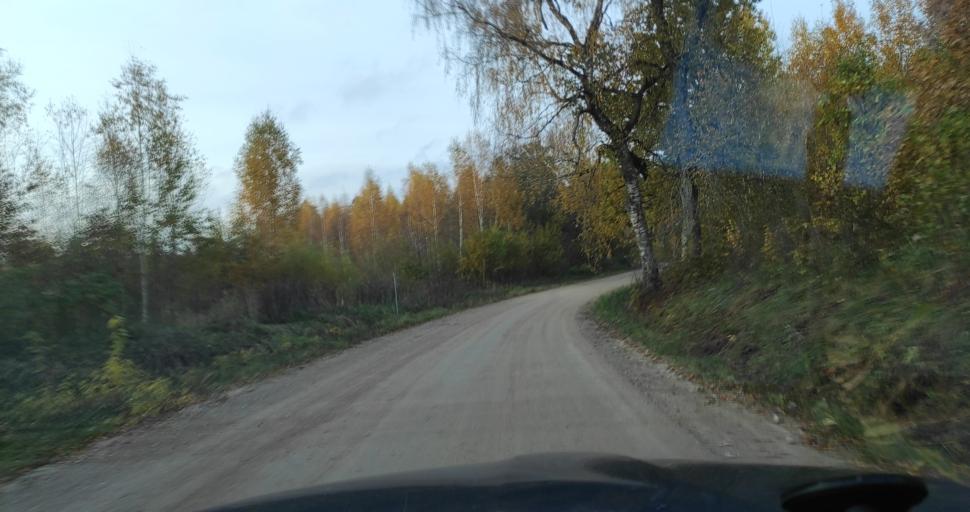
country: LV
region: Vainode
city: Vainode
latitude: 56.6281
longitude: 21.8172
